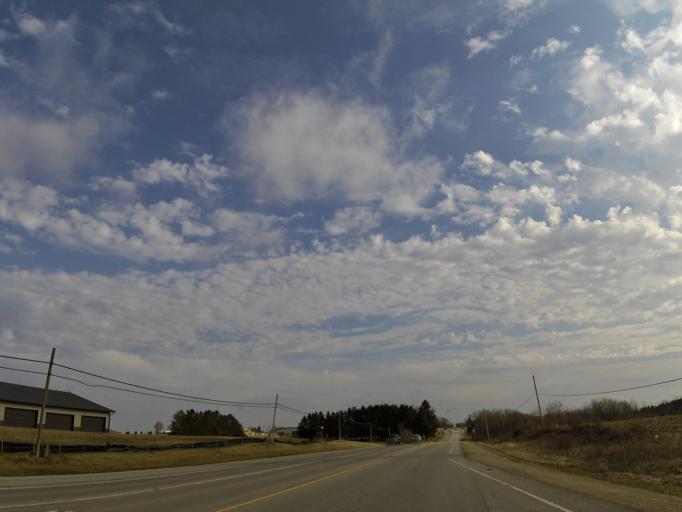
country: US
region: Wisconsin
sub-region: Pierce County
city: Ellsworth
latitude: 44.7464
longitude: -92.4871
